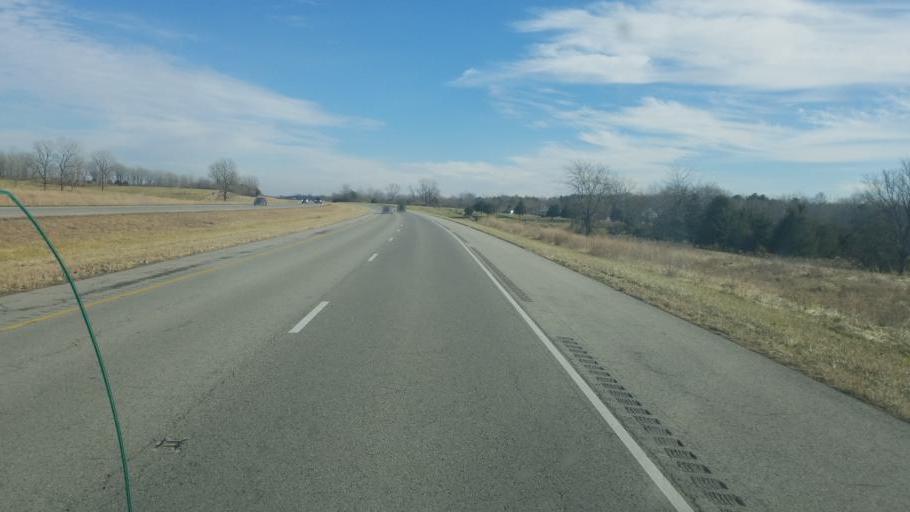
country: US
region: Illinois
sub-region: Williamson County
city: Marion
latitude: 37.7305
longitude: -88.7859
